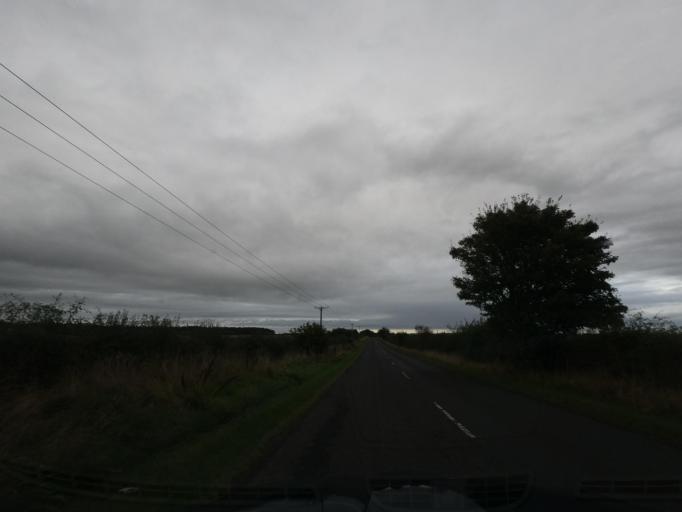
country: GB
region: England
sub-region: Northumberland
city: Ford
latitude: 55.6922
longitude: -2.0786
